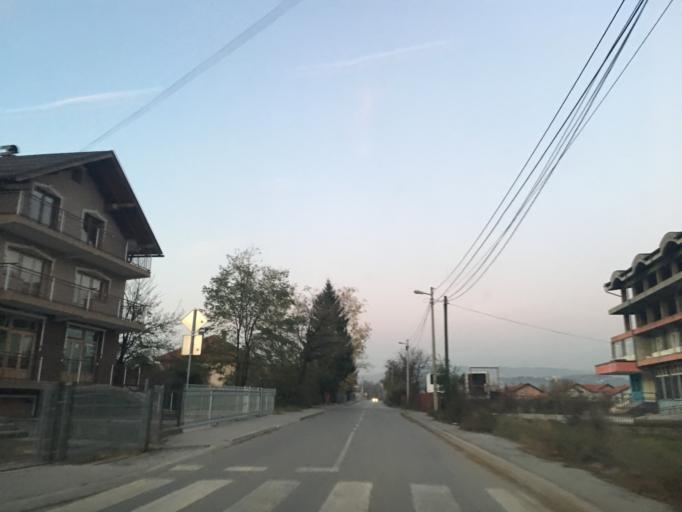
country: BA
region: Federation of Bosnia and Herzegovina
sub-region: Kanton Sarajevo
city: Sarajevo
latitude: 43.8162
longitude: 18.3284
